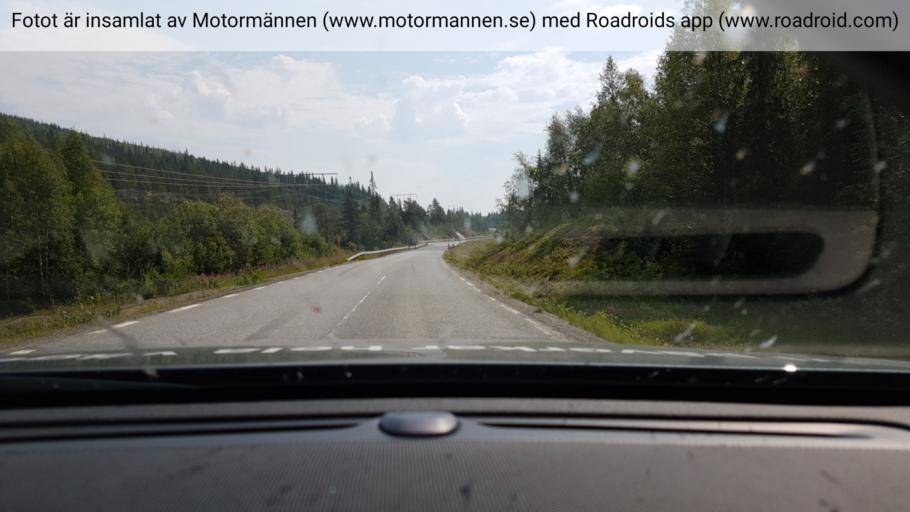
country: SE
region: Vaesterbotten
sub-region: Vilhelmina Kommun
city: Sjoberg
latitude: 65.4875
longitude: 15.8122
